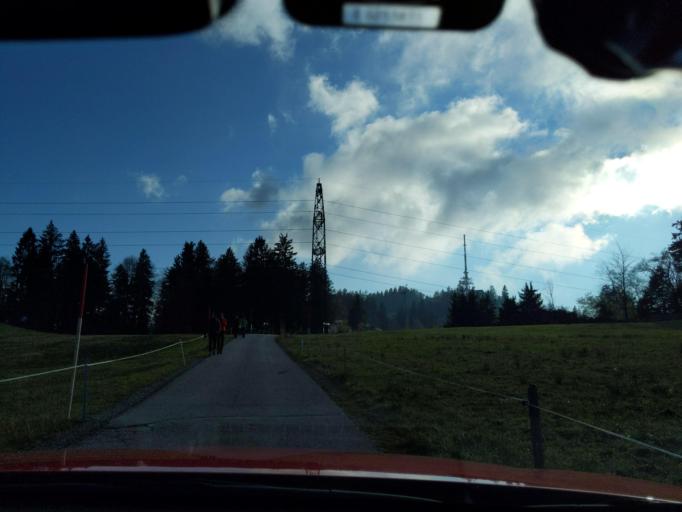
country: AT
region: Vorarlberg
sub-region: Politischer Bezirk Bregenz
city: Eichenberg
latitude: 47.5138
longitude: 9.7850
